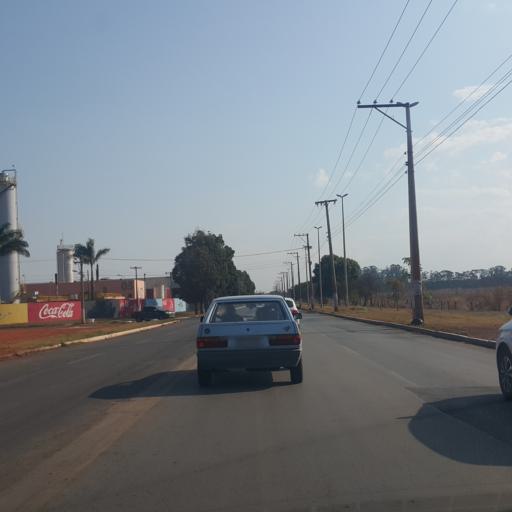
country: BR
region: Federal District
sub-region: Brasilia
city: Brasilia
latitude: -15.8693
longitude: -48.0386
